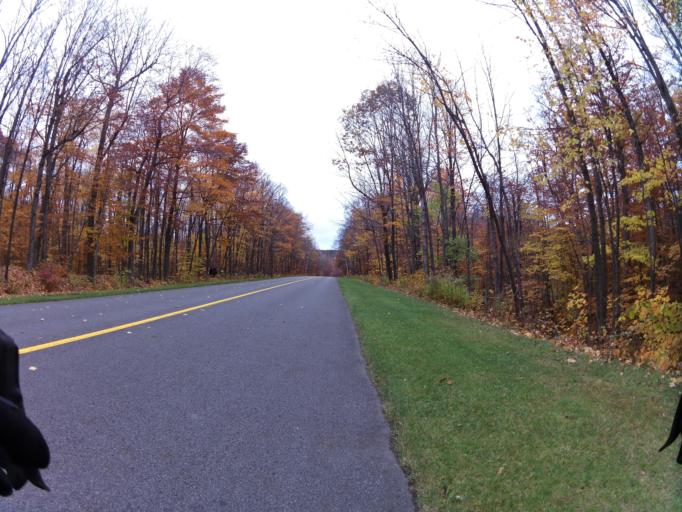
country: CA
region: Quebec
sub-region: Outaouais
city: Gatineau
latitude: 45.4869
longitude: -75.8307
